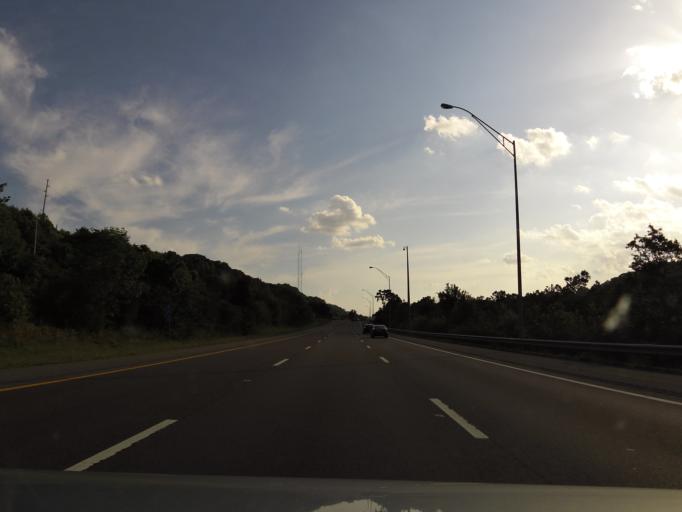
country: US
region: Tennessee
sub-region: Knox County
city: Knoxville
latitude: 36.0239
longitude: -83.9095
